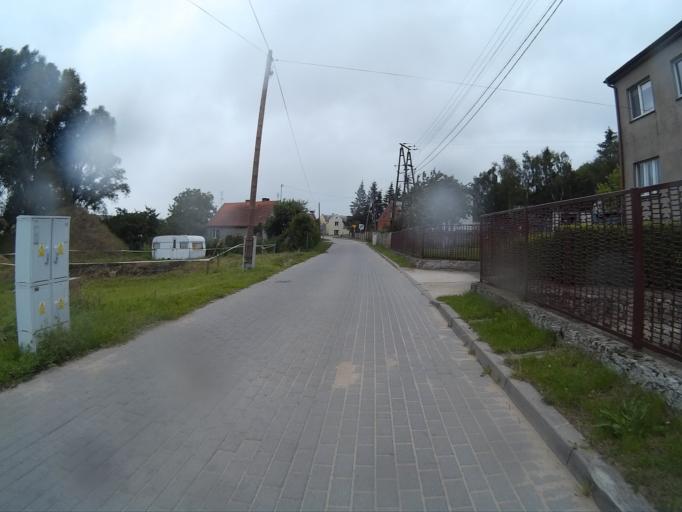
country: PL
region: Kujawsko-Pomorskie
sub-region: Powiat tucholski
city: Tuchola
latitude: 53.5947
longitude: 17.8853
